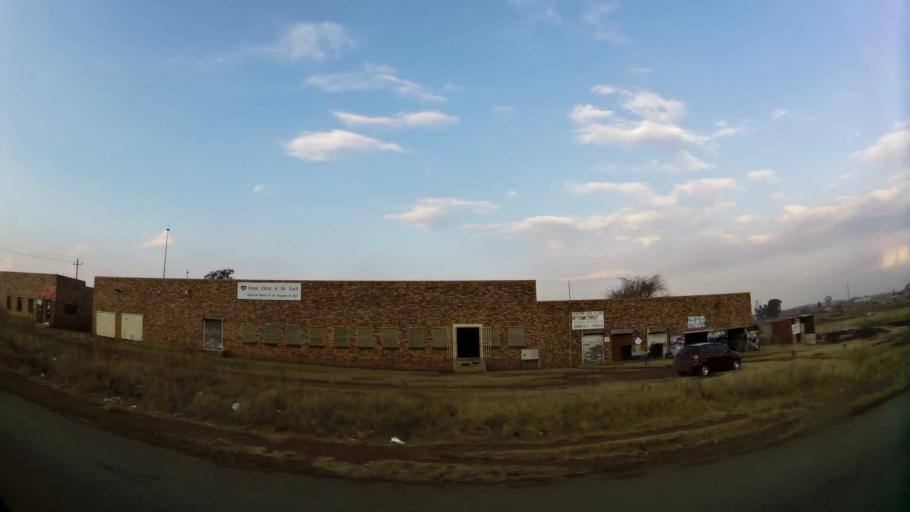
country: ZA
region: Gauteng
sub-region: City of Johannesburg Metropolitan Municipality
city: Orange Farm
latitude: -26.5411
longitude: 27.8333
